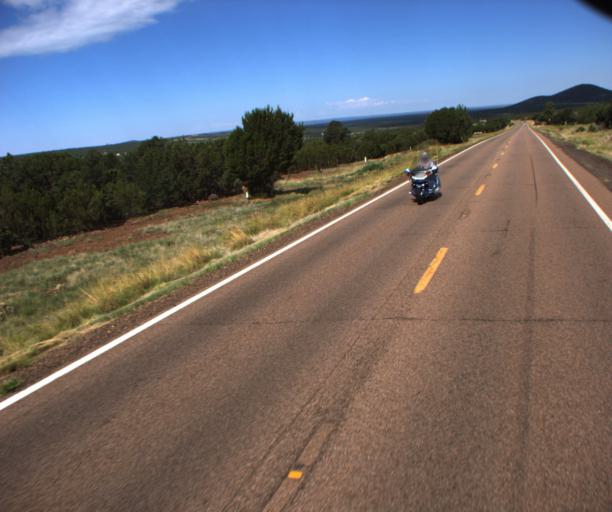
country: US
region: Arizona
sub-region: Navajo County
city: White Mountain Lake
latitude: 34.2826
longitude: -109.8117
